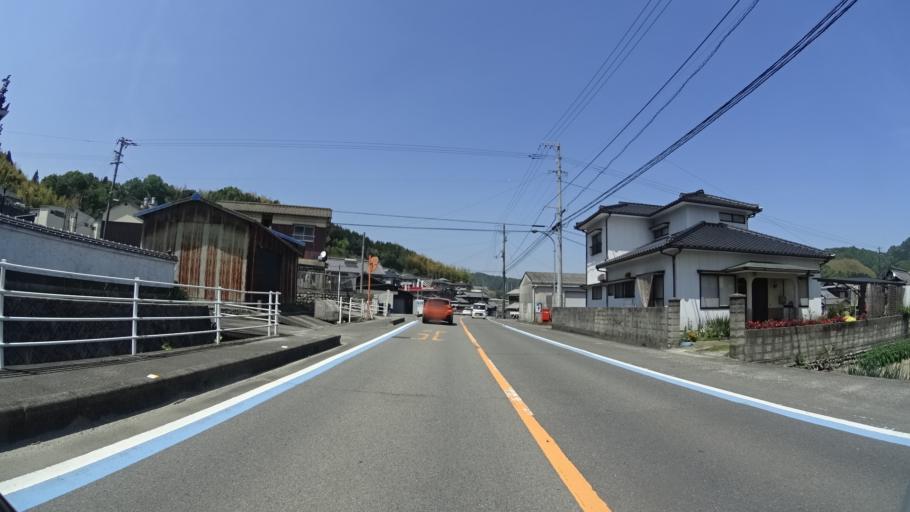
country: JP
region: Ehime
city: Hojo
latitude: 34.0118
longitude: 132.9379
